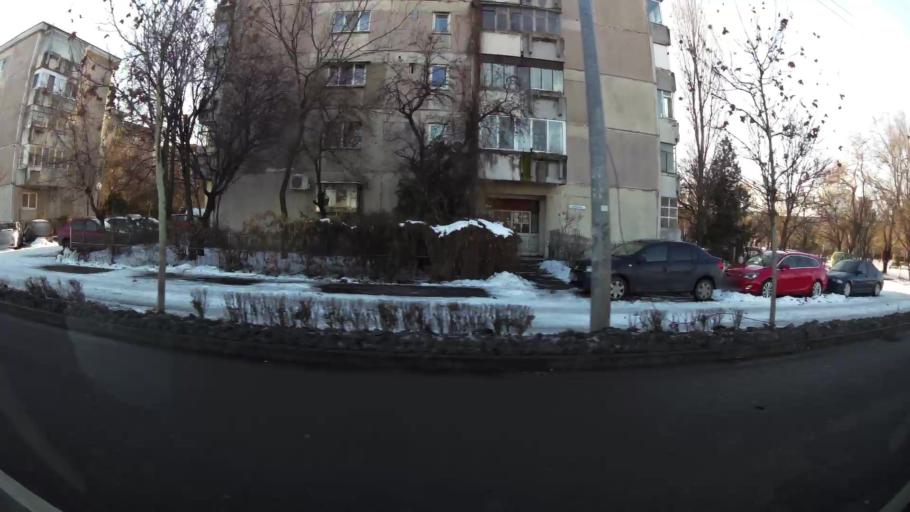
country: RO
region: Ilfov
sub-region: Comuna Fundeni-Dobroesti
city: Fundeni
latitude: 44.4546
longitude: 26.1483
